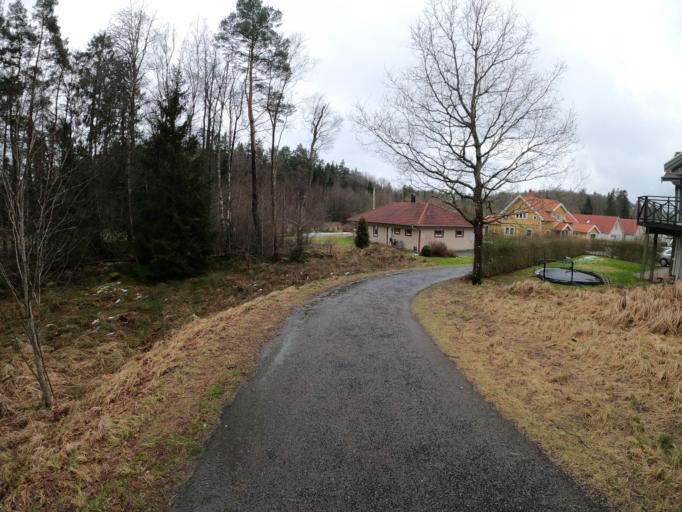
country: SE
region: Vaestra Goetaland
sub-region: Harryda Kommun
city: Molnlycke
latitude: 57.6433
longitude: 12.1100
